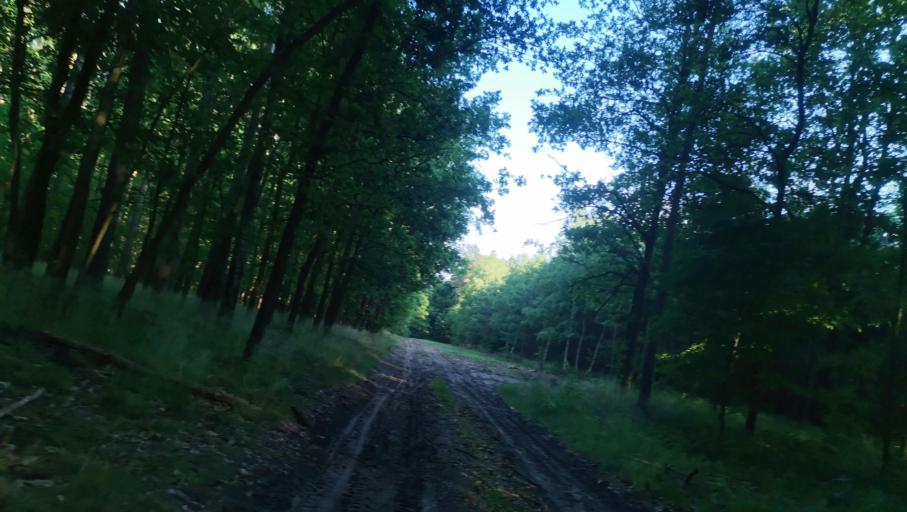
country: PL
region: Greater Poland Voivodeship
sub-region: Powiat jarocinski
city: Jarocin
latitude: 51.9832
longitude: 17.5438
